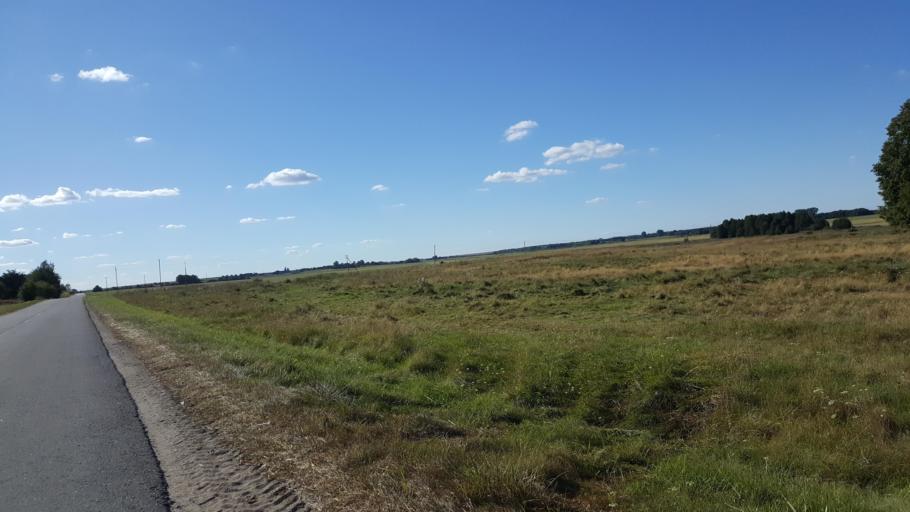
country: BY
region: Brest
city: Vysokaye
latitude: 52.3464
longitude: 23.5493
